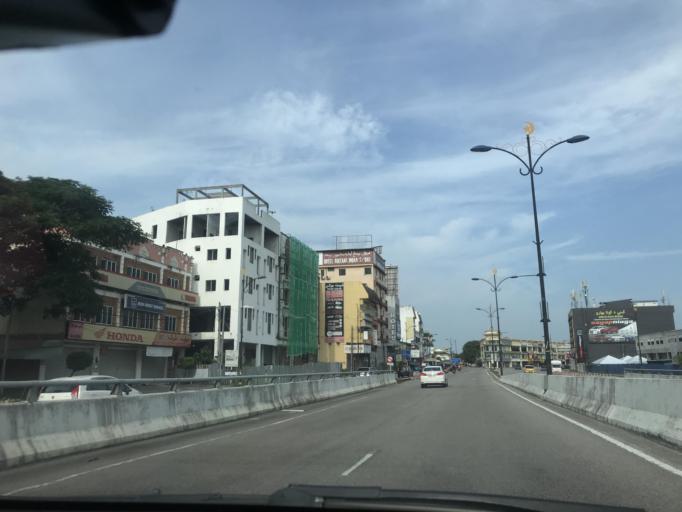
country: MY
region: Kelantan
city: Kota Bharu
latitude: 6.1168
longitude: 102.2452
